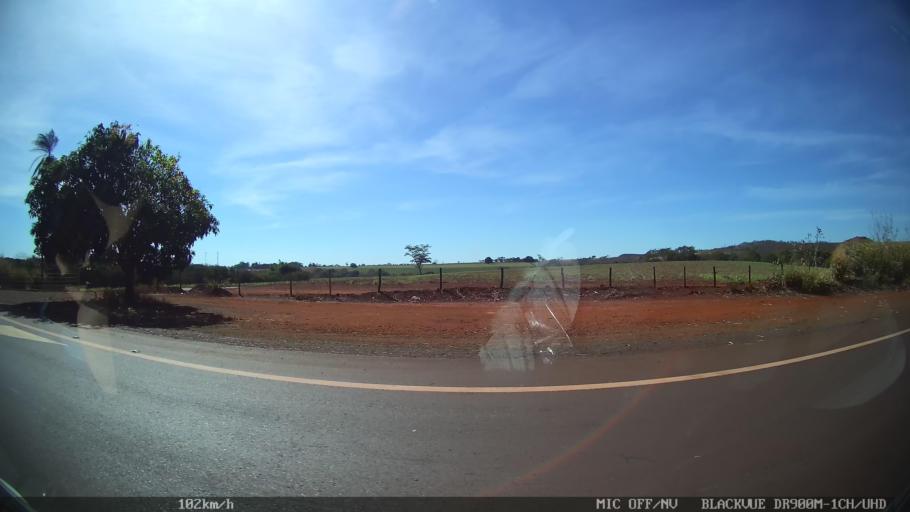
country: BR
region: Sao Paulo
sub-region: Sao Joaquim Da Barra
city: Sao Joaquim da Barra
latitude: -20.5271
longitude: -47.8359
